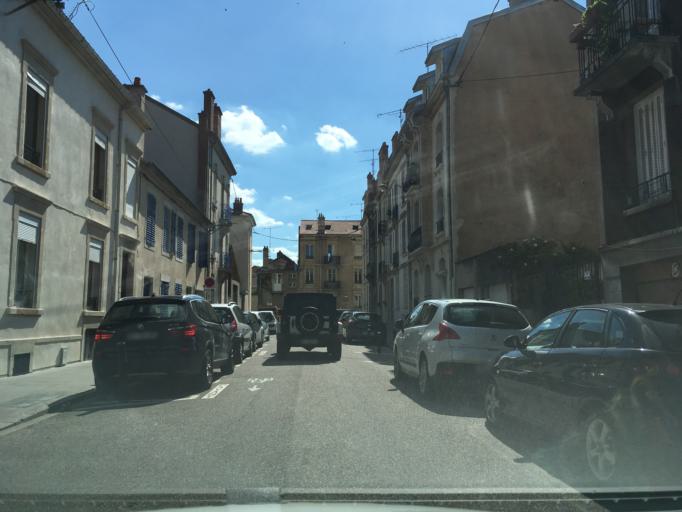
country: FR
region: Lorraine
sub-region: Departement de Meurthe-et-Moselle
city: Malzeville
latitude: 48.7030
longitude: 6.1783
